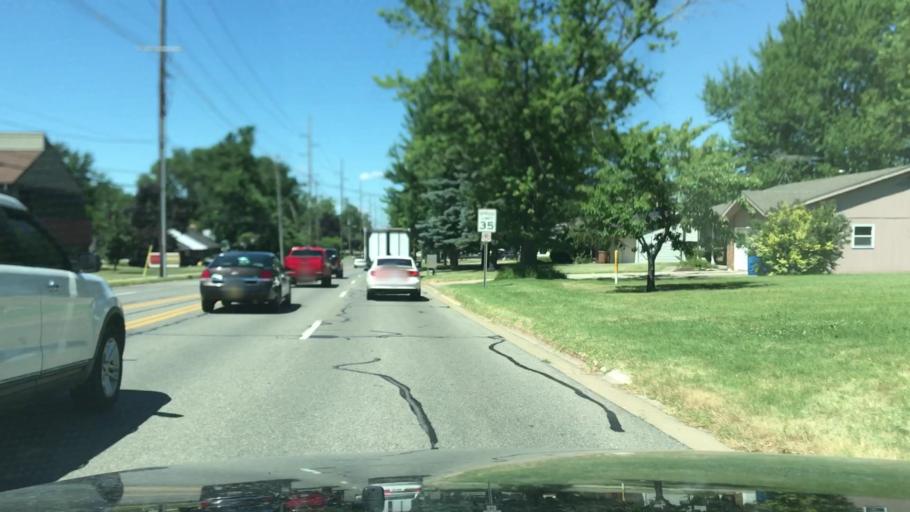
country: US
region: Michigan
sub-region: Ottawa County
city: Holland
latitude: 42.7842
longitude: -86.0775
